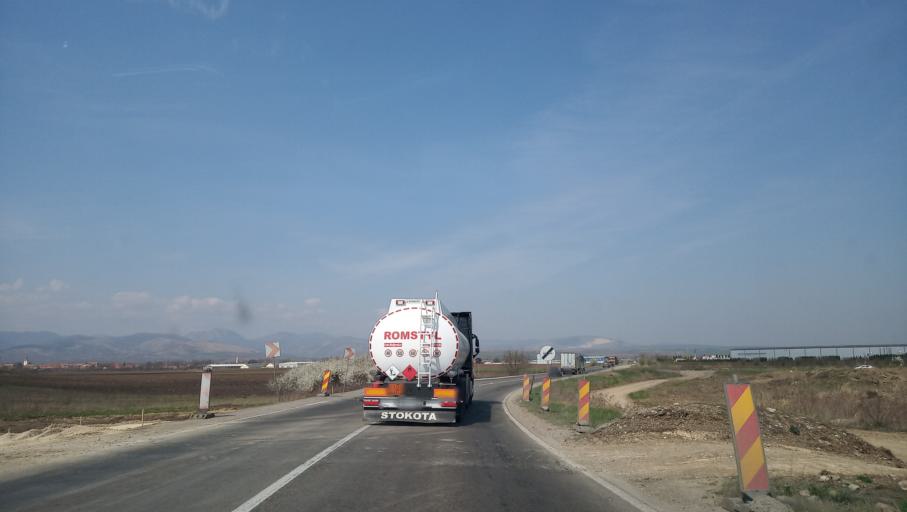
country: RO
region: Alba
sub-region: Comuna Santimbru
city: Santimbru
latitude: 46.1484
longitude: 23.6443
